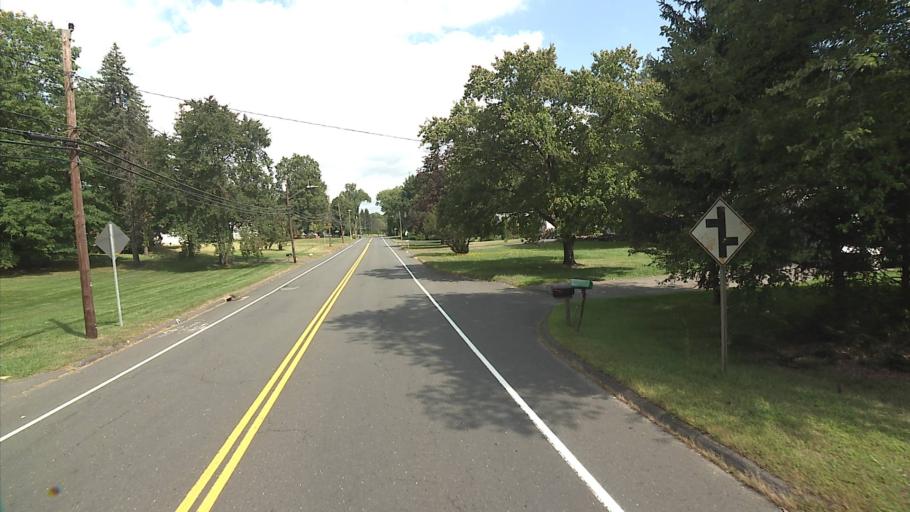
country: US
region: Connecticut
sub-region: Hartford County
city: Blue Hills
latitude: 41.8455
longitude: -72.7443
